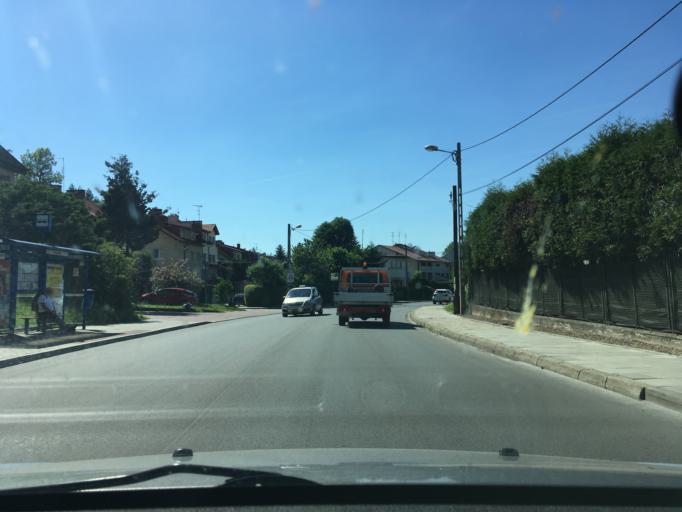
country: PL
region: Lesser Poland Voivodeship
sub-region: Krakow
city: Krakow
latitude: 50.0608
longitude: 19.8917
